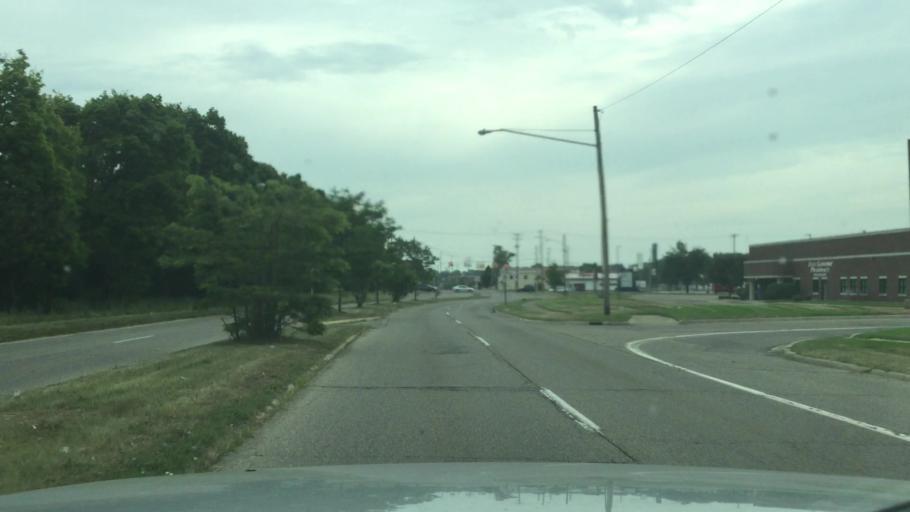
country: US
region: Michigan
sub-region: Genesee County
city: Flint
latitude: 43.0257
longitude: -83.6577
